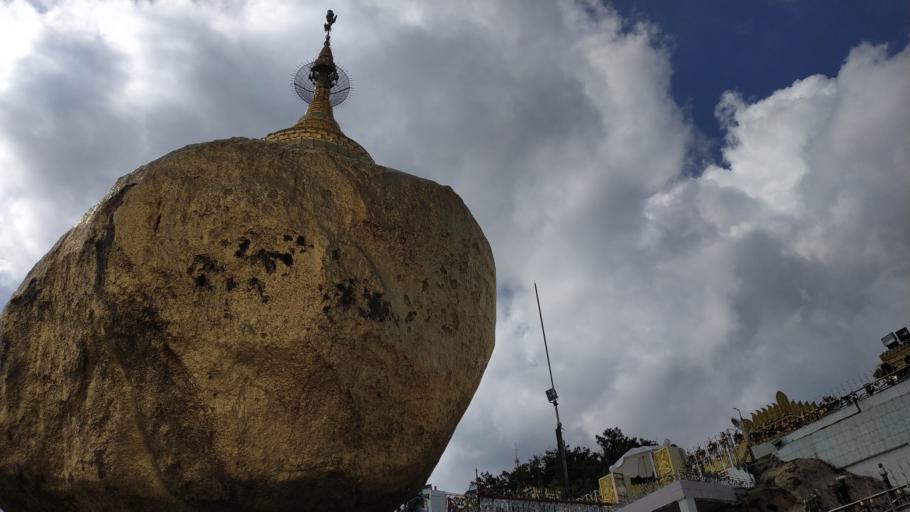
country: MM
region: Mon
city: Kyaikto
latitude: 17.4815
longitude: 97.0982
